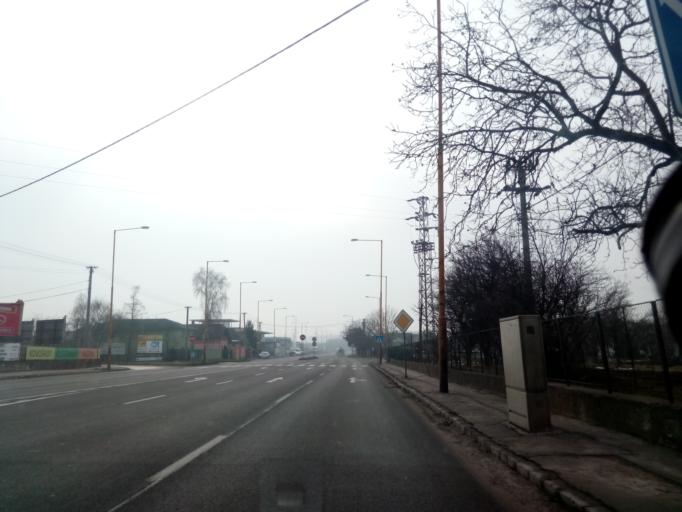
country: SK
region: Kosicky
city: Kosice
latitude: 48.6722
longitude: 21.2704
